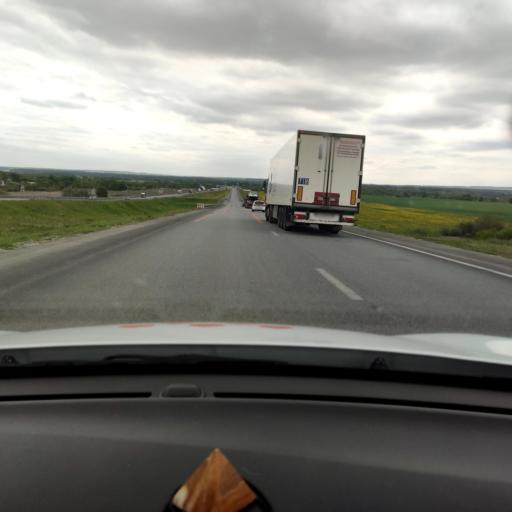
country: RU
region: Tatarstan
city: Pestretsy
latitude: 55.7071
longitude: 49.5608
